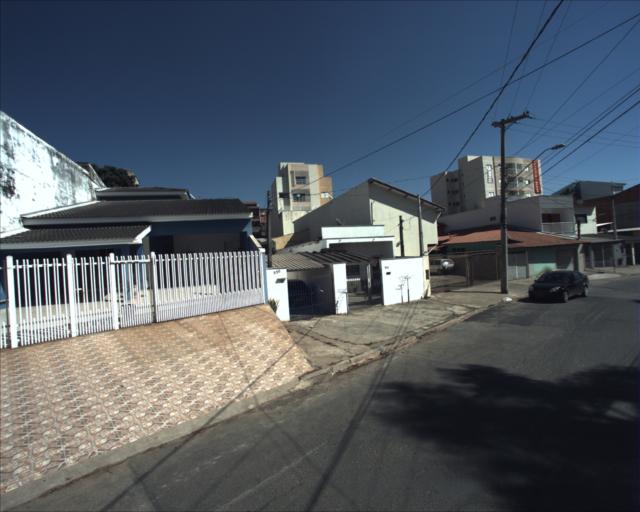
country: BR
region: Sao Paulo
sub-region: Sorocaba
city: Sorocaba
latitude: -23.4937
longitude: -47.4187
